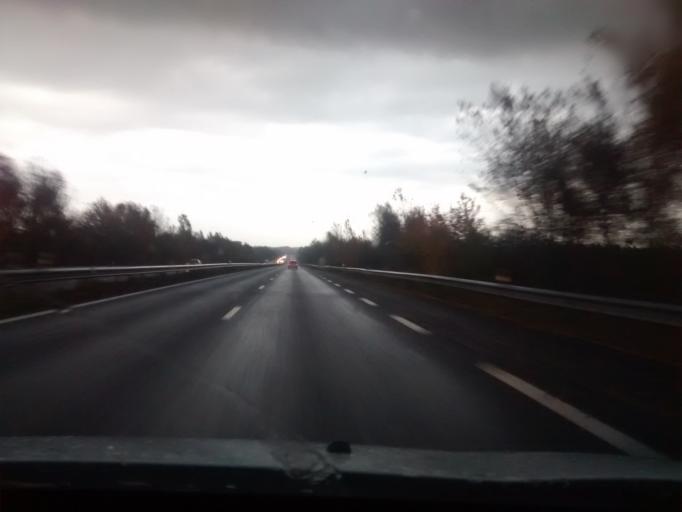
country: FR
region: Brittany
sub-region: Departement d'Ille-et-Vilaine
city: Pleugueneuc
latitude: 48.3841
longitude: -1.9006
